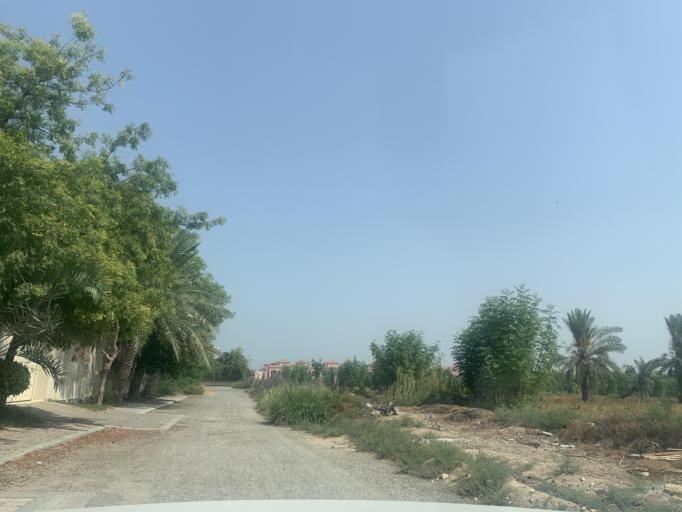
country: BH
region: Central Governorate
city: Madinat Hamad
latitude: 26.1658
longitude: 50.4591
